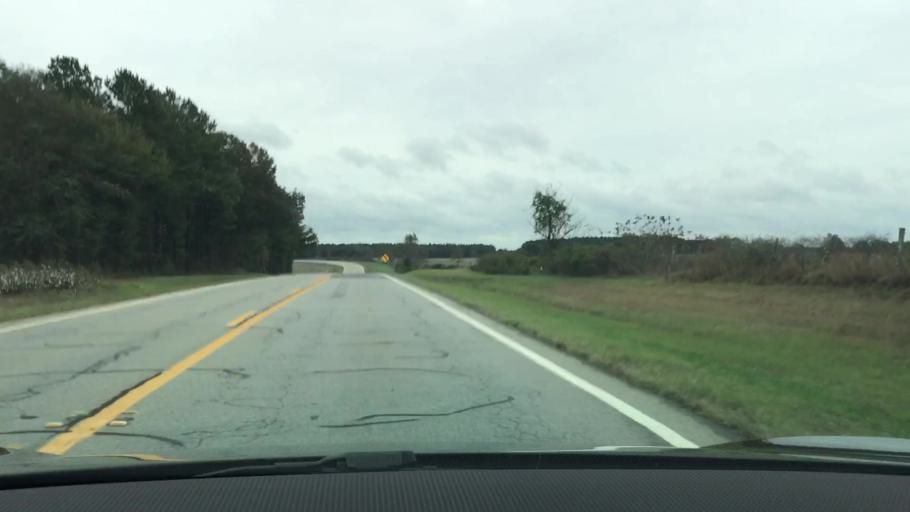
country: US
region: Georgia
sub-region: Warren County
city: Warrenton
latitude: 33.3616
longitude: -82.5971
